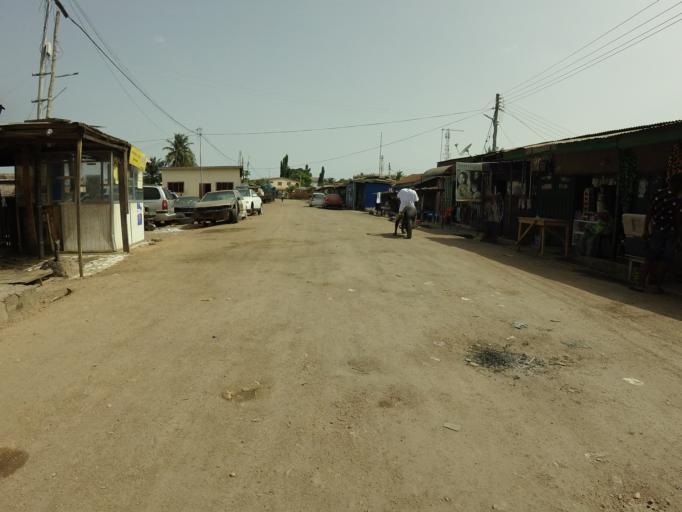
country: GH
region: Greater Accra
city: Dome
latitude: 5.6155
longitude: -0.2395
